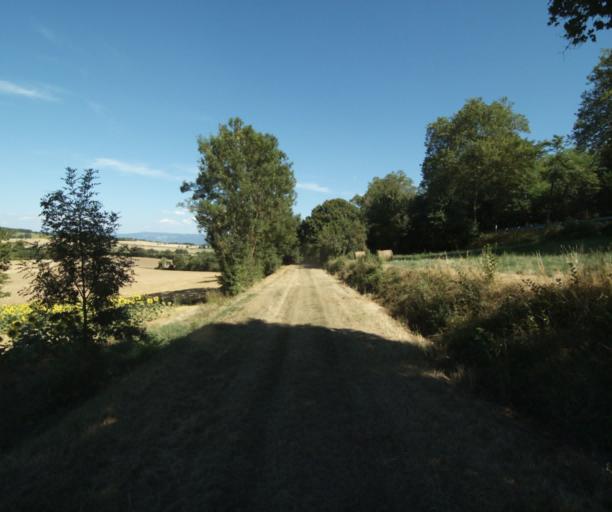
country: FR
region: Midi-Pyrenees
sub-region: Departement de la Haute-Garonne
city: Saint-Felix-Lauragais
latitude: 43.4945
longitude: 1.8984
